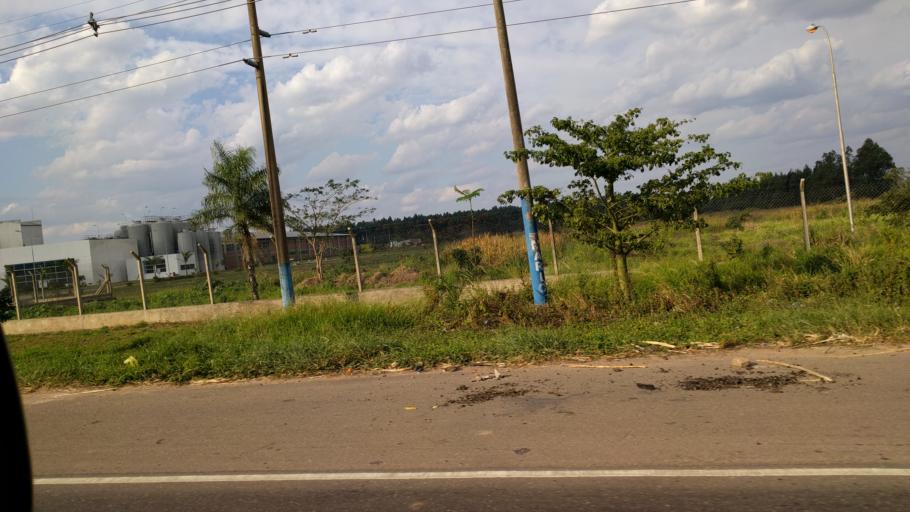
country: BO
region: Santa Cruz
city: La Belgica
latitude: -17.5603
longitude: -63.1593
